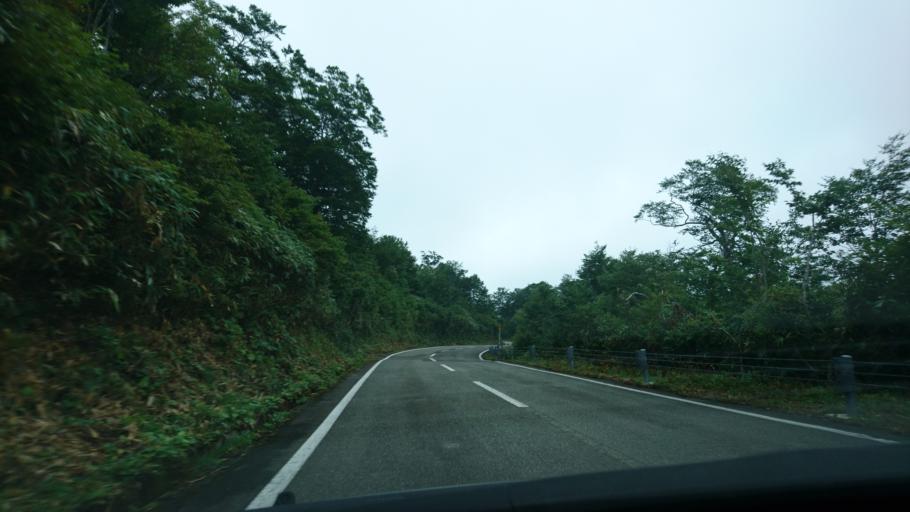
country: JP
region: Akita
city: Yuzawa
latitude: 38.9798
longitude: 140.7477
